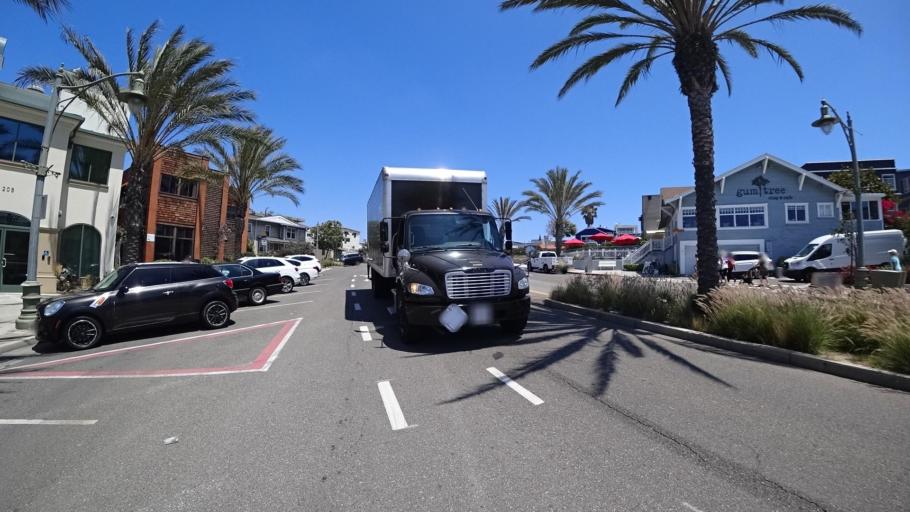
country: US
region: California
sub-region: Los Angeles County
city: Hermosa Beach
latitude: 33.8632
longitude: -118.3990
